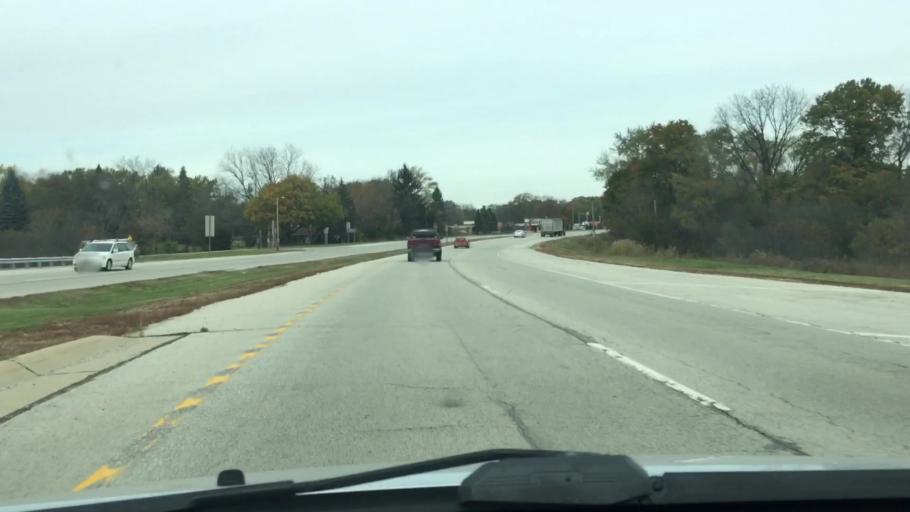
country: US
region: Wisconsin
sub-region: Milwaukee County
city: Hales Corners
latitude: 42.9150
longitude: -88.0454
